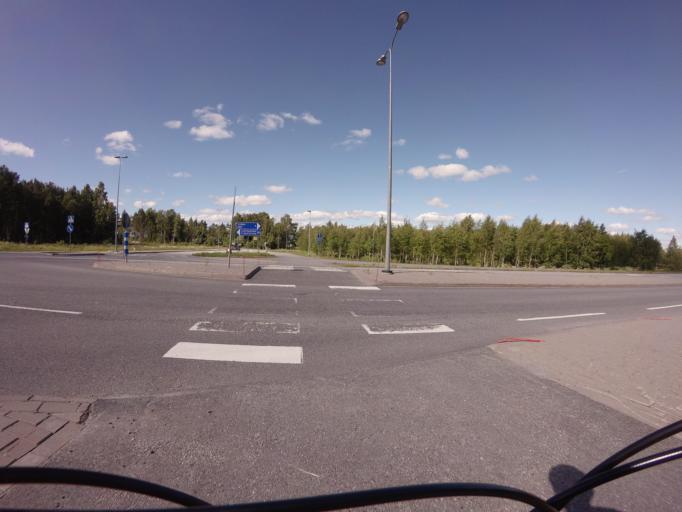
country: FI
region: Varsinais-Suomi
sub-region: Turku
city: Turku
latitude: 60.5096
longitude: 22.2898
